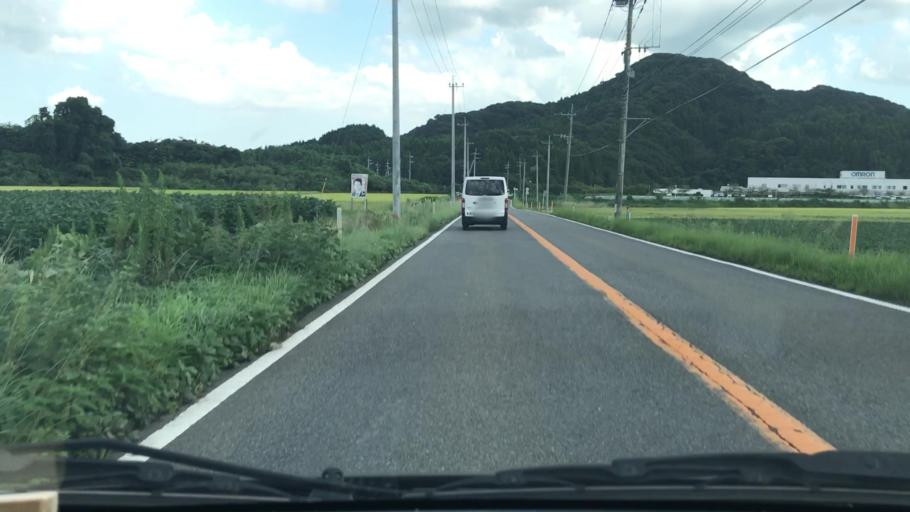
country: JP
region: Saga Prefecture
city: Takeocho-takeo
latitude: 33.2255
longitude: 130.0303
